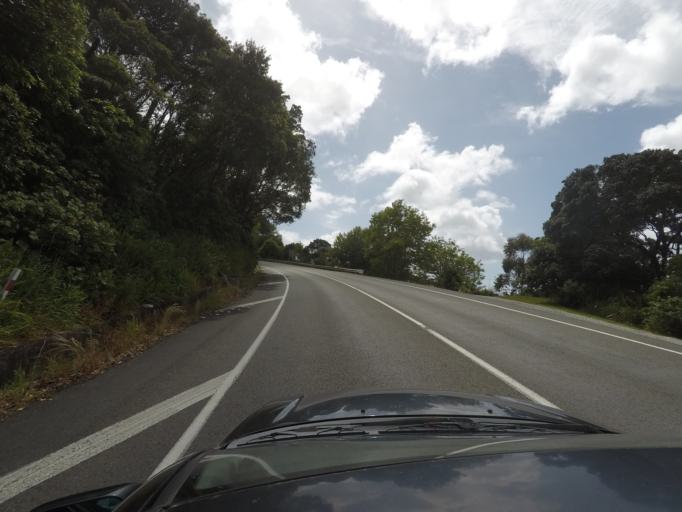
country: NZ
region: Auckland
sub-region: Auckland
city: Rothesay Bay
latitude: -36.5731
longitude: 174.6927
